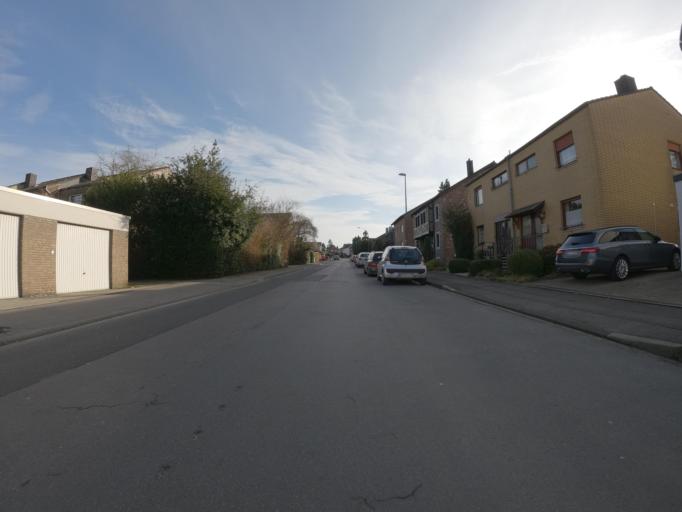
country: DE
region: North Rhine-Westphalia
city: Stolberg
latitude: 50.7463
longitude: 6.1582
